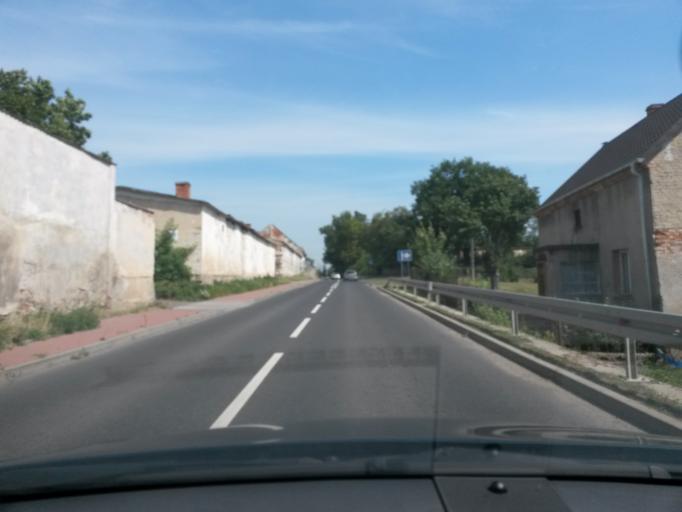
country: PL
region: Lower Silesian Voivodeship
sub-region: Powiat legnicki
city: Legnickie Pole
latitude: 51.1713
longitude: 16.3325
